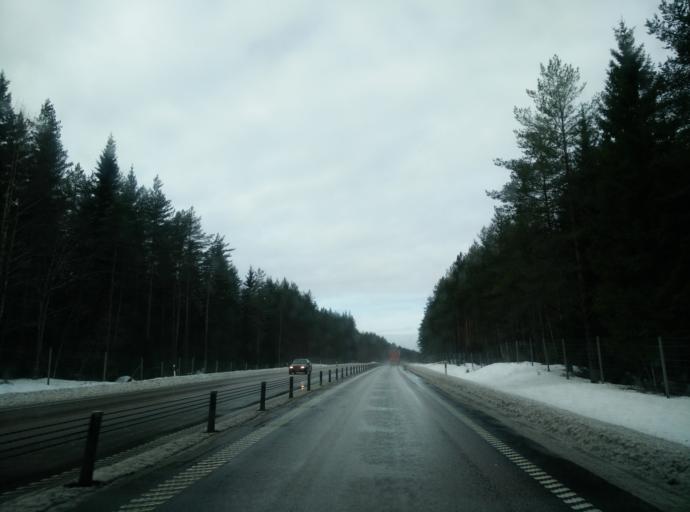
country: SE
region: Dalarna
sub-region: Hedemora Kommun
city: Langshyttan
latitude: 60.5546
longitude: 16.0849
